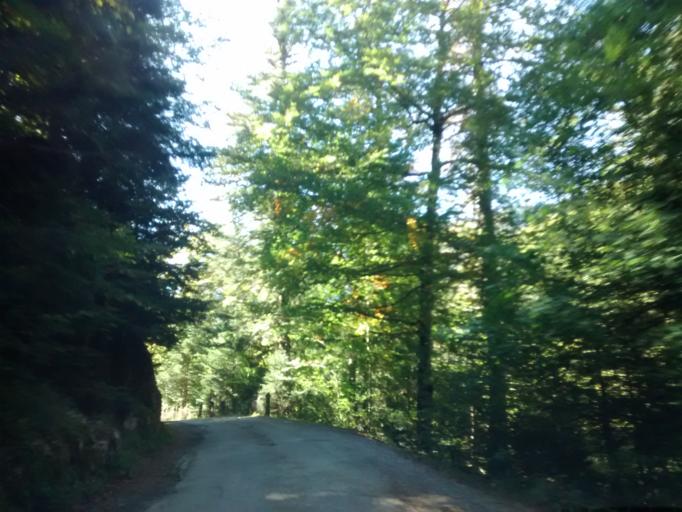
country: ES
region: Aragon
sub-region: Provincia de Huesca
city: Aragues del Puerto
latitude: 42.8440
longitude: -0.7103
